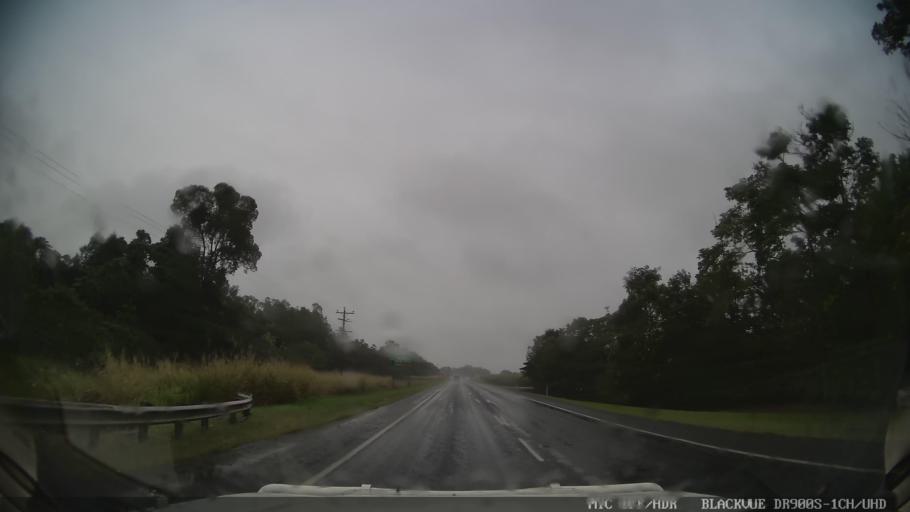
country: AU
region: Queensland
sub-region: Cassowary Coast
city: Innisfail
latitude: -17.7527
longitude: 146.0278
